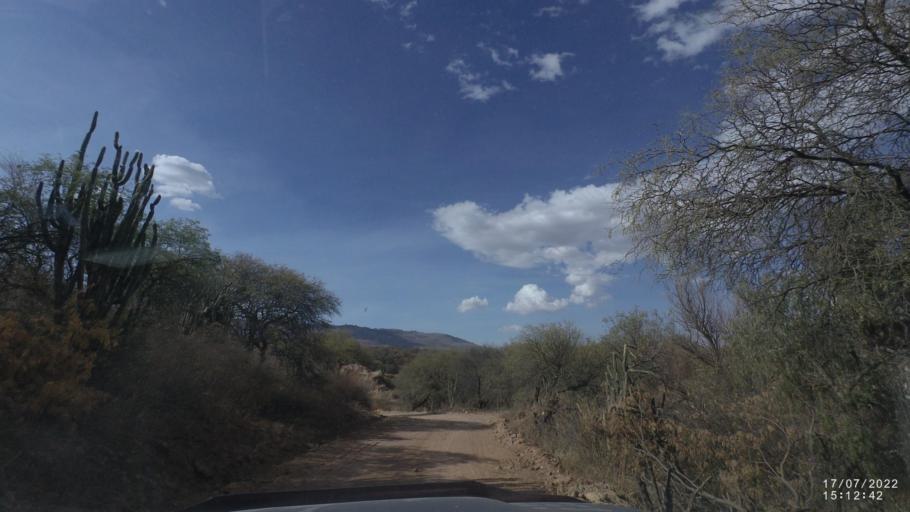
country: BO
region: Cochabamba
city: Capinota
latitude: -17.5688
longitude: -66.2631
